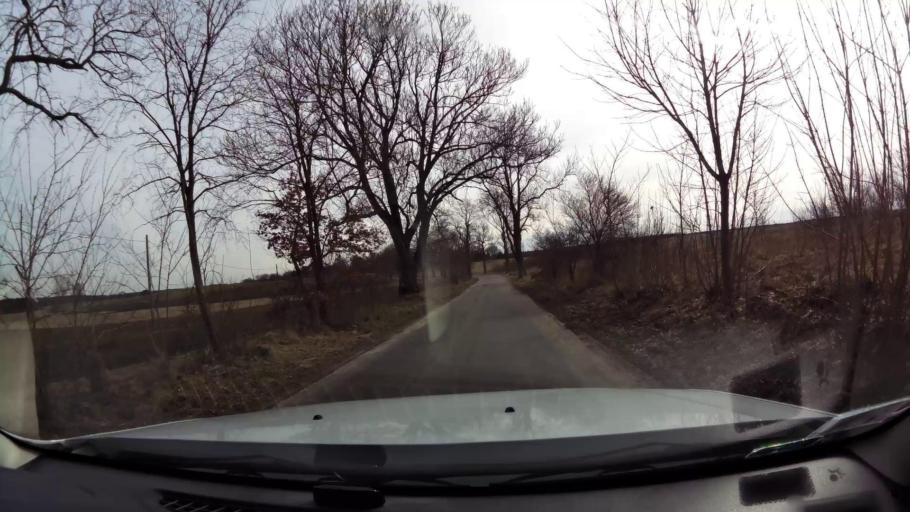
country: PL
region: West Pomeranian Voivodeship
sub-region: Powiat stargardzki
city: Insko
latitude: 53.4564
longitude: 15.6132
